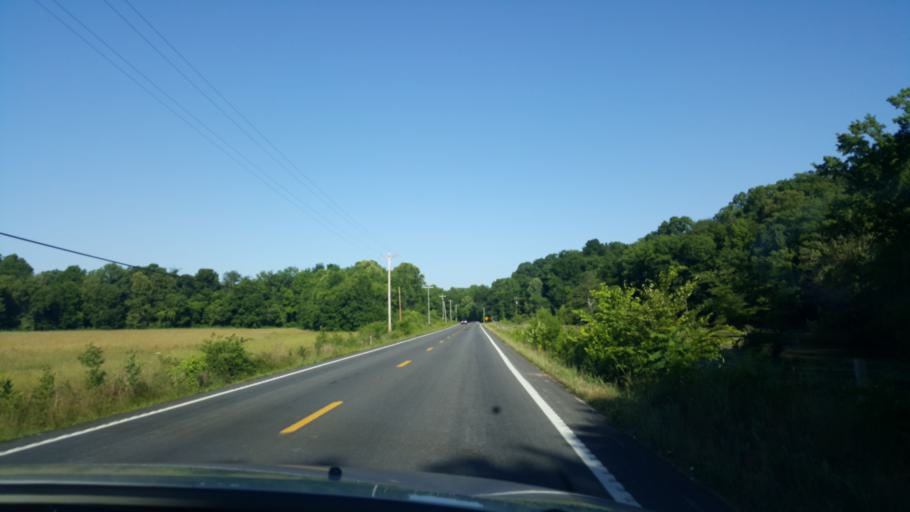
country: US
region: Tennessee
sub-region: Lawrence County
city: Lawrenceburg
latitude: 35.3988
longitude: -87.3800
